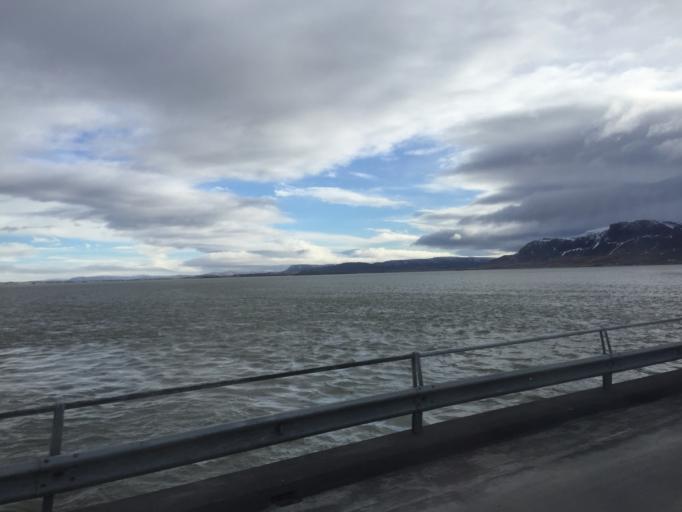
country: IS
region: West
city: Borgarnes
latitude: 64.5352
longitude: -21.8965
